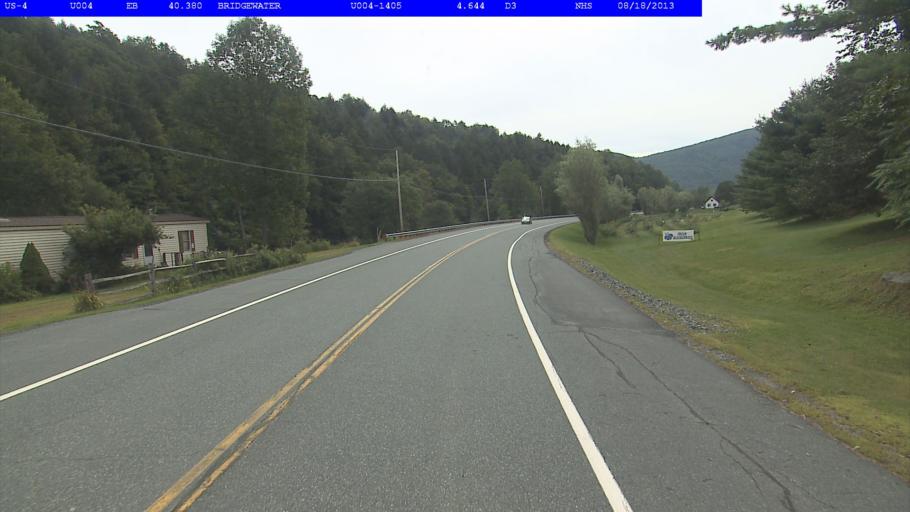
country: US
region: Vermont
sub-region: Windsor County
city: Woodstock
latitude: 43.5980
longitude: -72.6703
